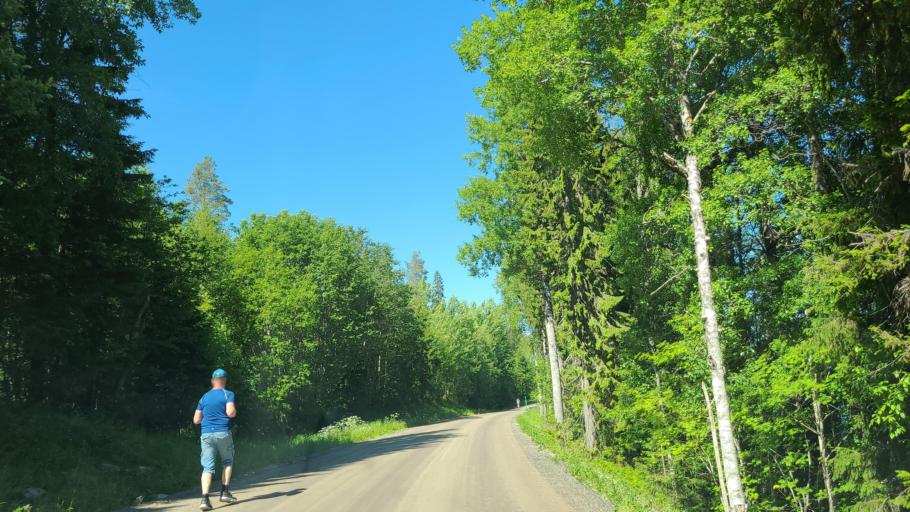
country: SE
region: Vaesternorrland
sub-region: OErnskoeldsviks Kommun
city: Husum
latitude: 63.6339
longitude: 19.0595
